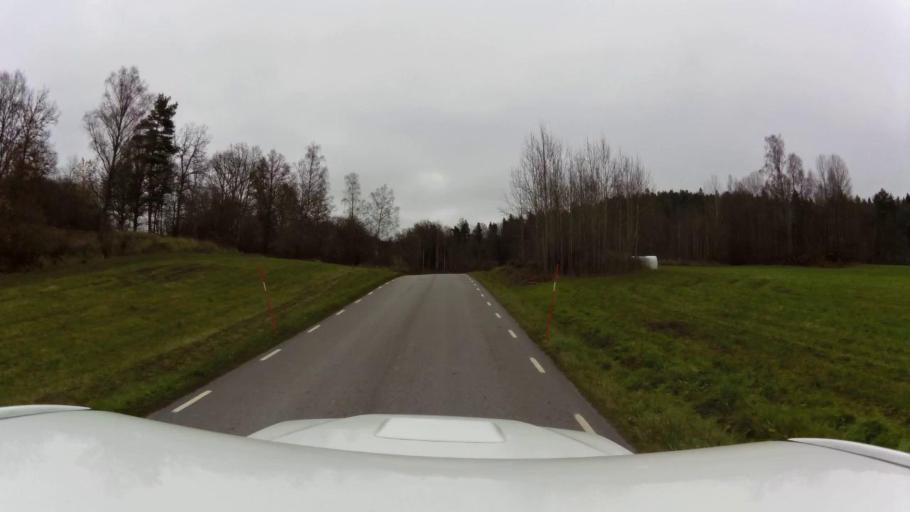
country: SE
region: OEstergoetland
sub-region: Kinda Kommun
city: Rimforsa
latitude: 58.1424
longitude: 15.6438
